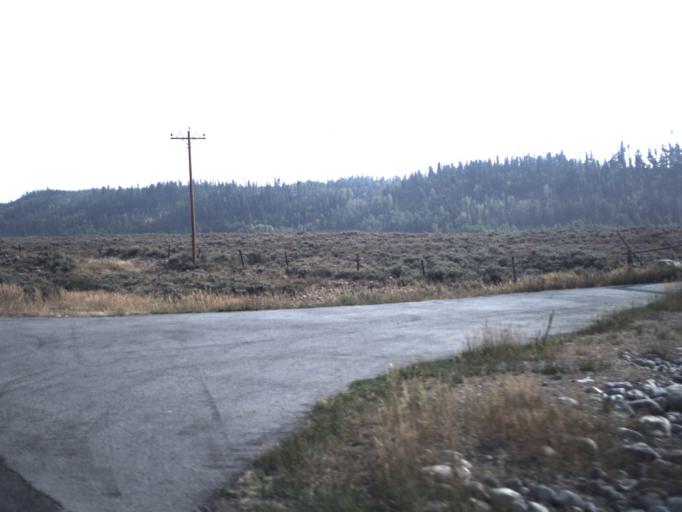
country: US
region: Wyoming
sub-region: Uinta County
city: Evanston
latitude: 40.9436
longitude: -110.8383
